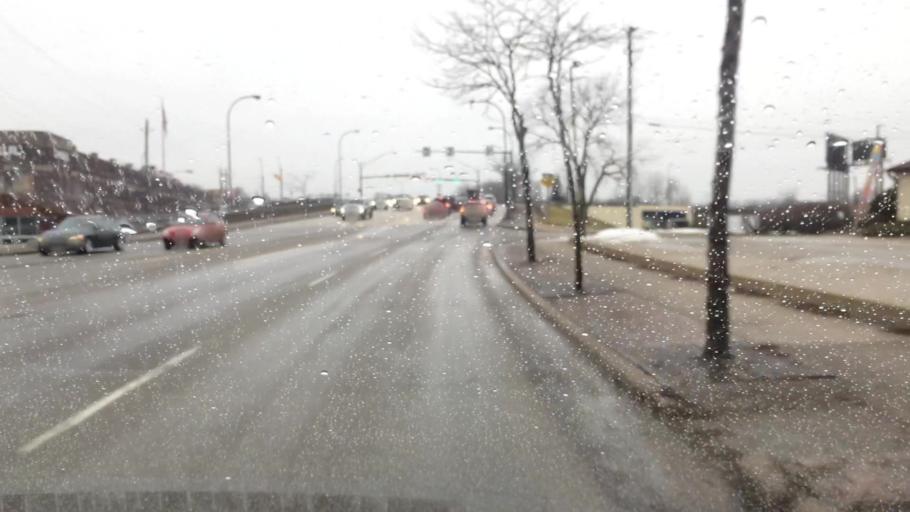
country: US
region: Ohio
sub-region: Summit County
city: Cuyahoga Falls
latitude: 41.1024
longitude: -81.4864
